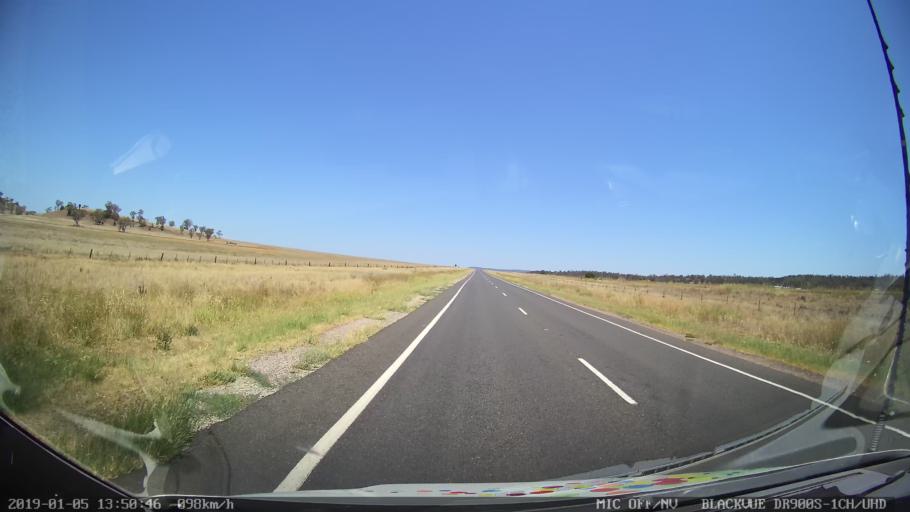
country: AU
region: New South Wales
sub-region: Gunnedah
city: Gunnedah
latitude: -31.0348
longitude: 150.2753
